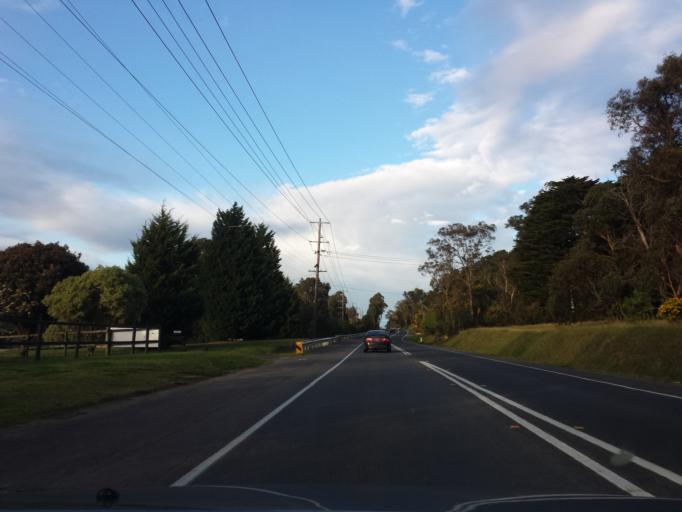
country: AU
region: Victoria
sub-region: Yarra Ranges
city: Lysterfield
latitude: -37.9277
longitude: 145.2752
